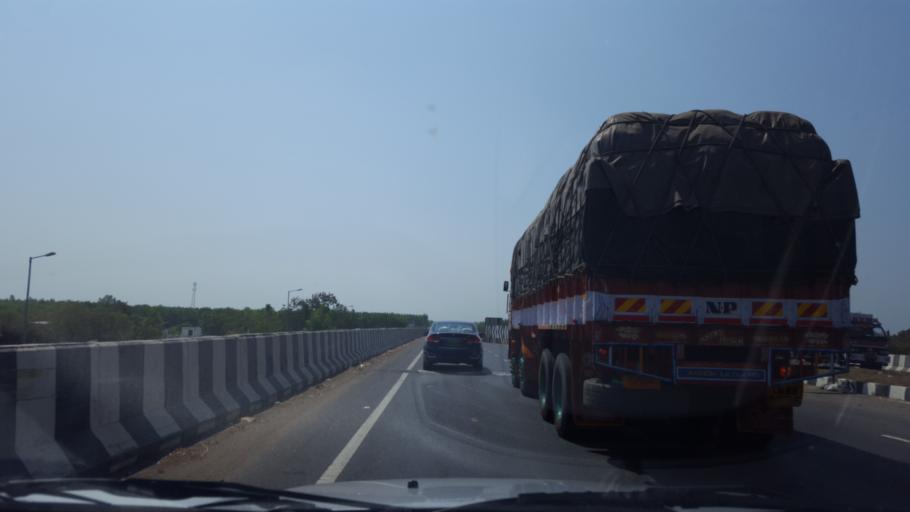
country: IN
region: Andhra Pradesh
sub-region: Prakasam
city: Addanki
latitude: 15.8043
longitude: 80.0408
